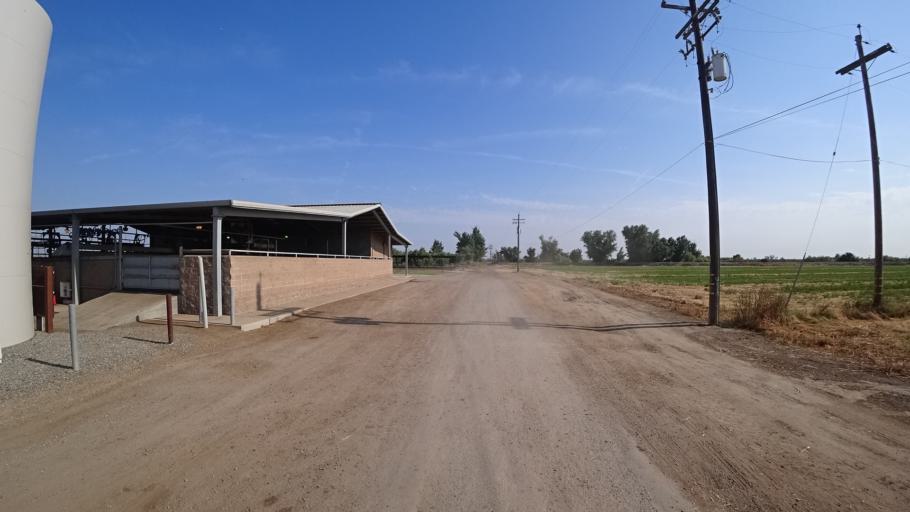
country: US
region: California
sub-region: Fresno County
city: Riverdale
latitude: 36.3850
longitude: -119.8341
